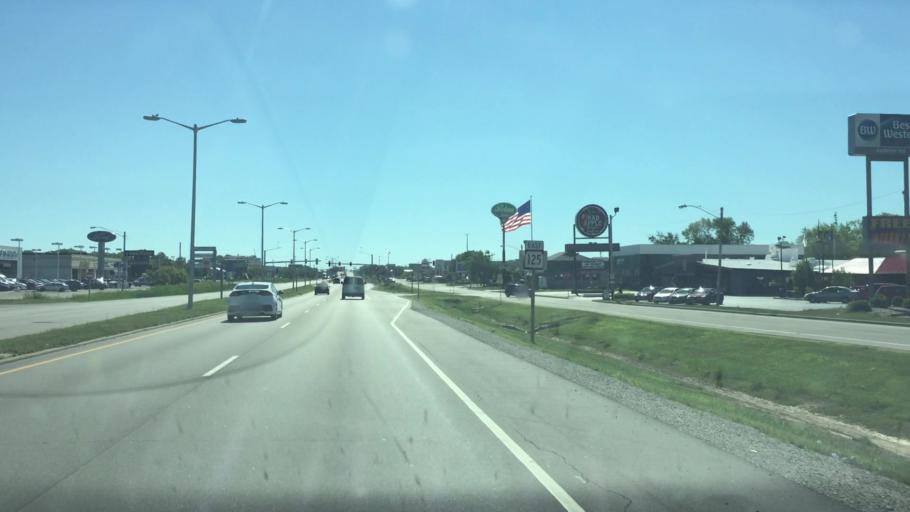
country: US
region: Wisconsin
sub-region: Outagamie County
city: Appleton
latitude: 44.2617
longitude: -88.4544
